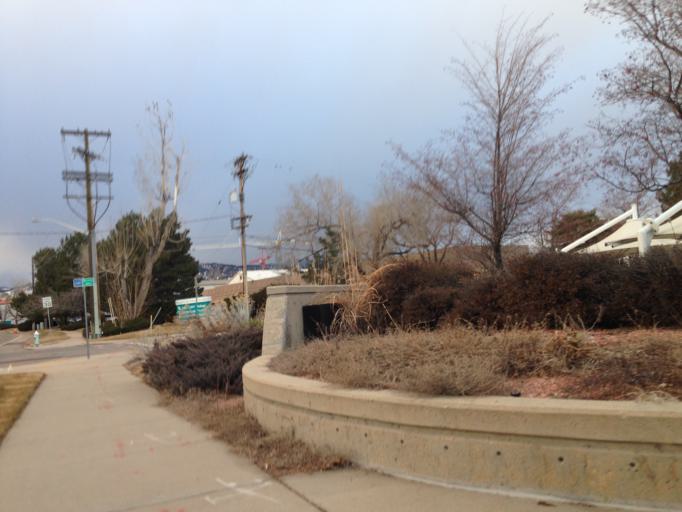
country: US
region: Colorado
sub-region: Boulder County
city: Boulder
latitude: 40.0200
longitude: -105.2491
